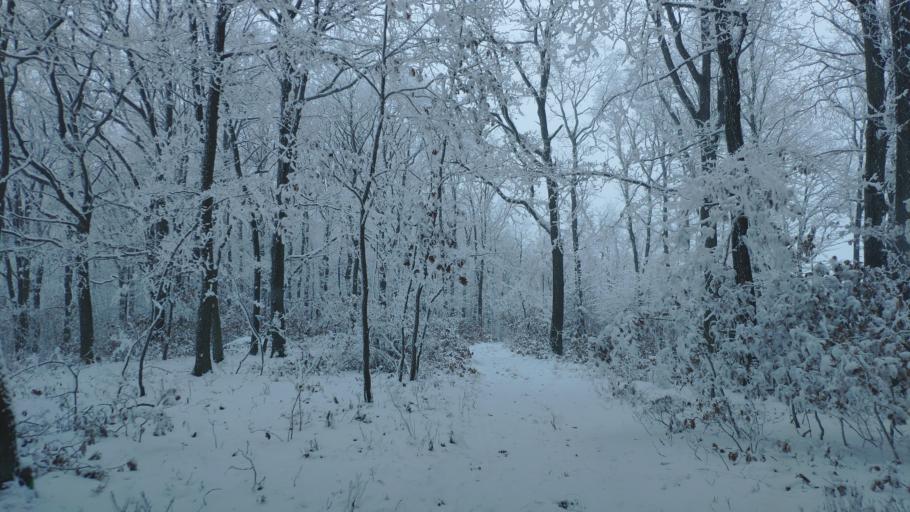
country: SK
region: Kosicky
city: Kosice
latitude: 48.6542
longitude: 21.1834
